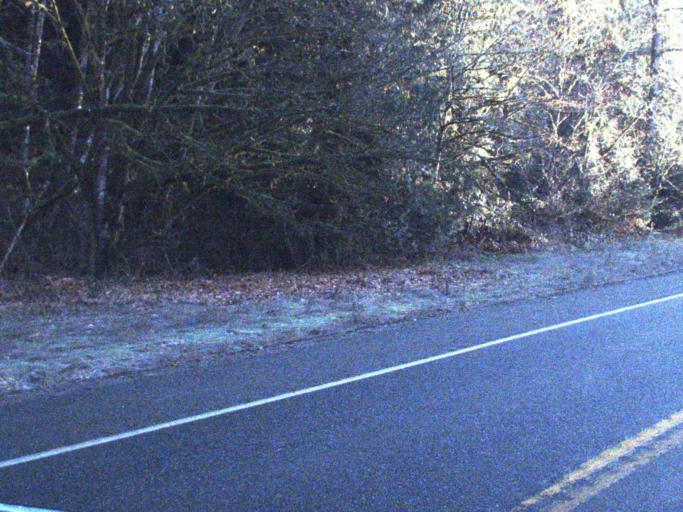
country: US
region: Washington
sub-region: Snohomish County
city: Darrington
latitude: 48.5126
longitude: -121.6682
